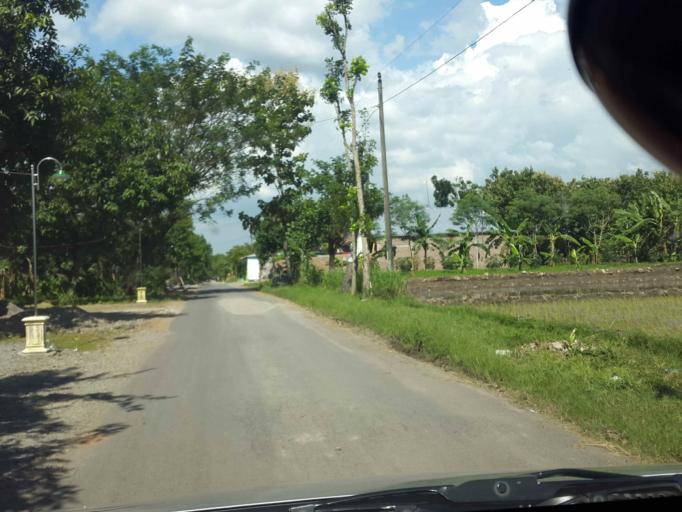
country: ID
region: Central Java
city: Sragen
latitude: -7.4522
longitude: 111.1061
